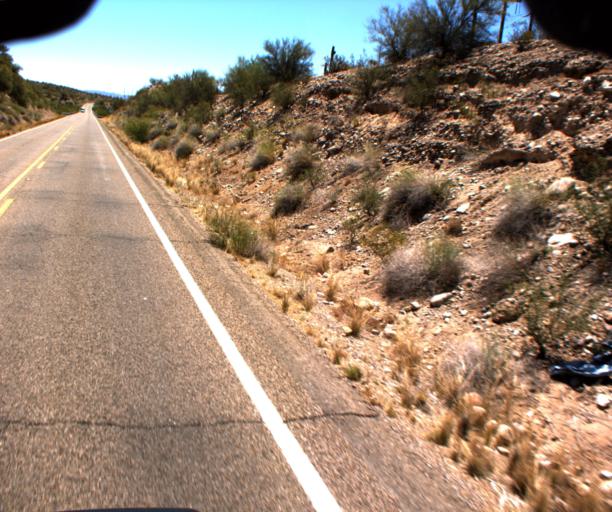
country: US
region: Arizona
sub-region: Pinal County
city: Kearny
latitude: 33.0290
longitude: -110.8723
